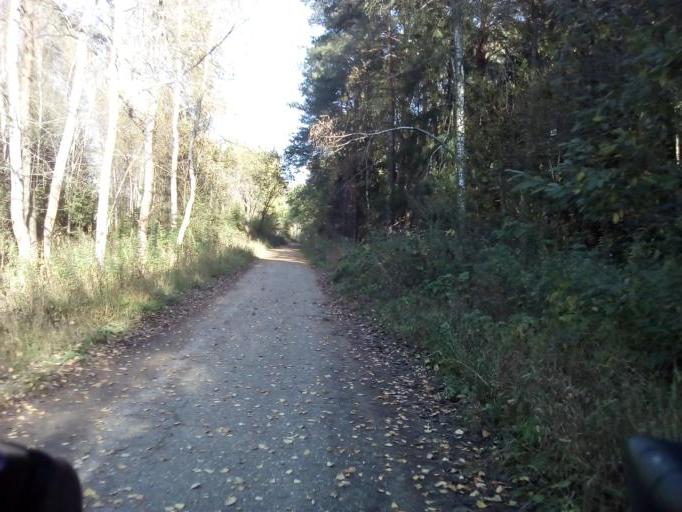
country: RU
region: Moskovskaya
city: Malyshevo
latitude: 55.5597
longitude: 38.3238
